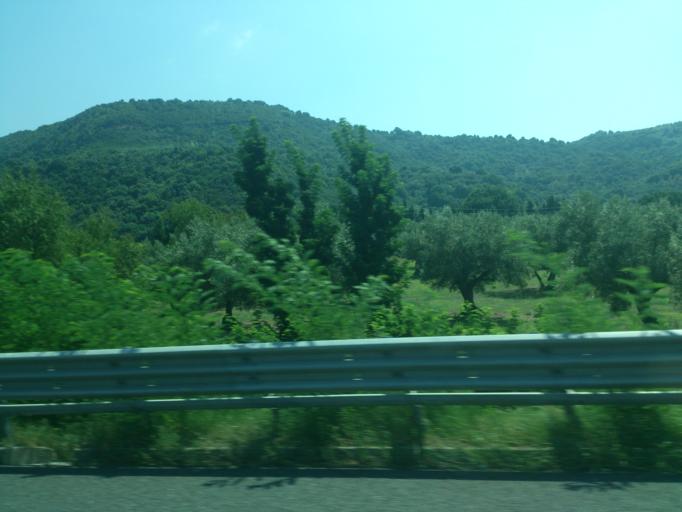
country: IT
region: Calabria
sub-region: Provincia di Vibo-Valentia
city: Francavilla Angitola
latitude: 38.7977
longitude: 16.2267
